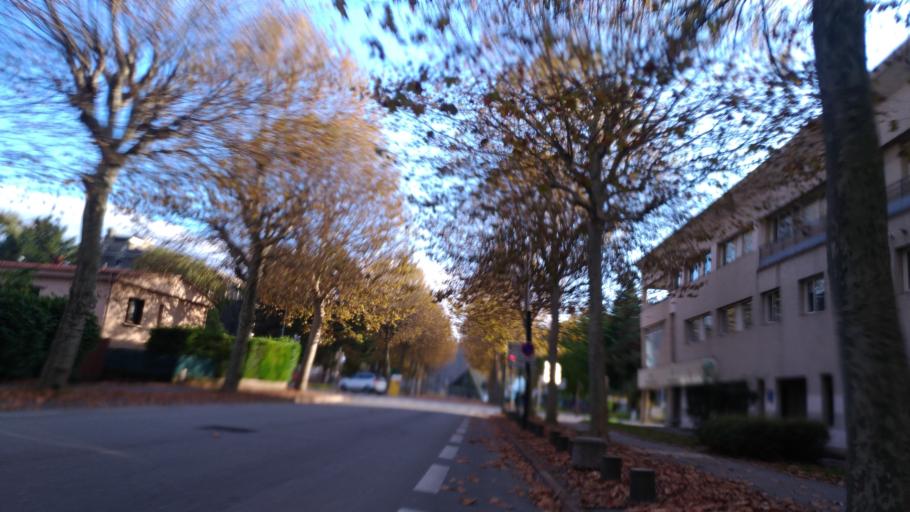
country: FR
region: Rhone-Alpes
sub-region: Departement de l'Isere
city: Fontaine
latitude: 45.1927
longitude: 5.6874
